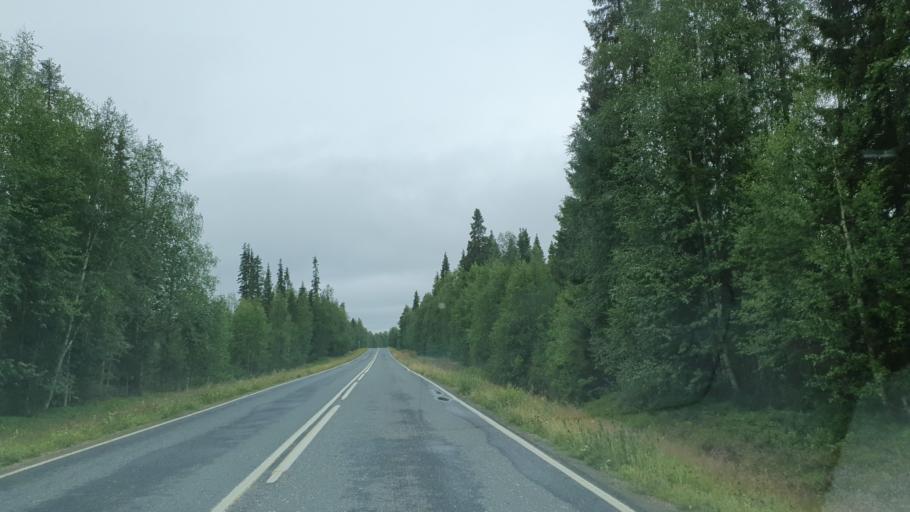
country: FI
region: Lapland
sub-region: Itae-Lappi
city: Pelkosenniemi
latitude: 67.2292
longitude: 27.3511
